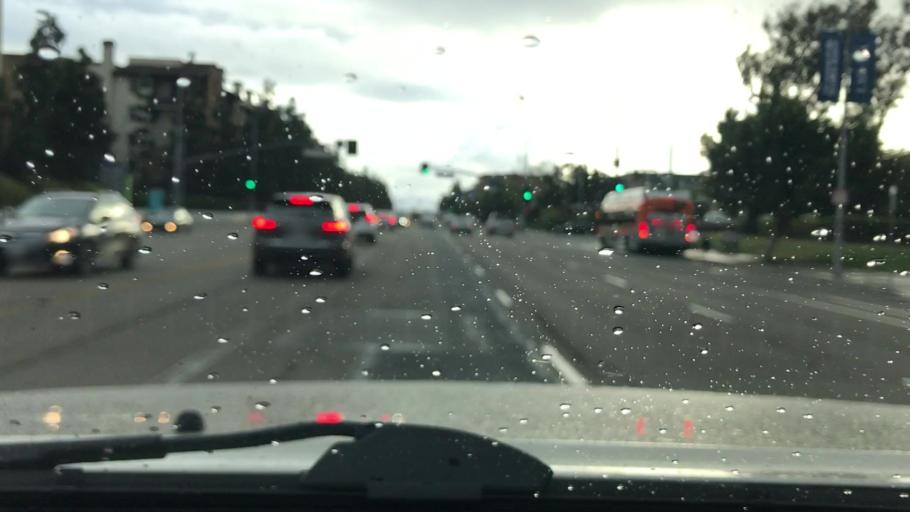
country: US
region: California
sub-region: Los Angeles County
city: Marina del Rey
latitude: 33.9750
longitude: -118.4237
